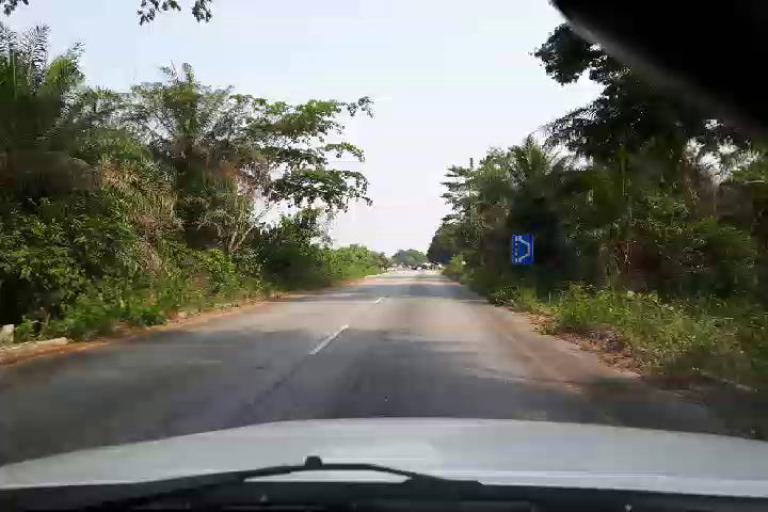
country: SL
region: Southern Province
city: Baiima
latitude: 8.1361
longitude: -11.8883
